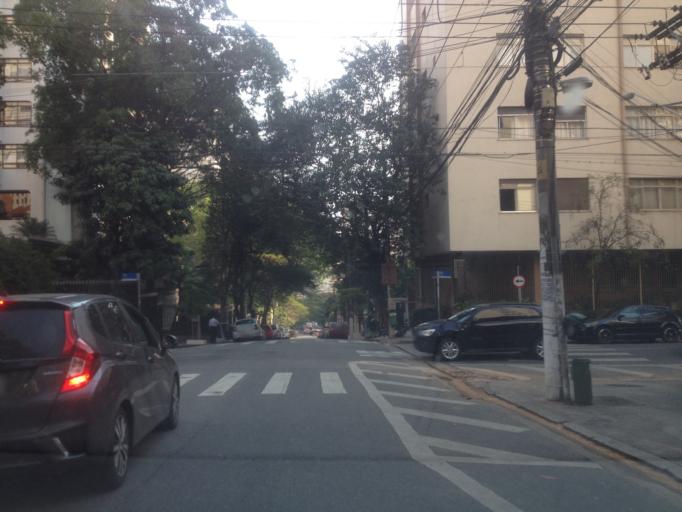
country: BR
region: Sao Paulo
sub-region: Sao Paulo
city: Sao Paulo
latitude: -23.5615
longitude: -46.6619
